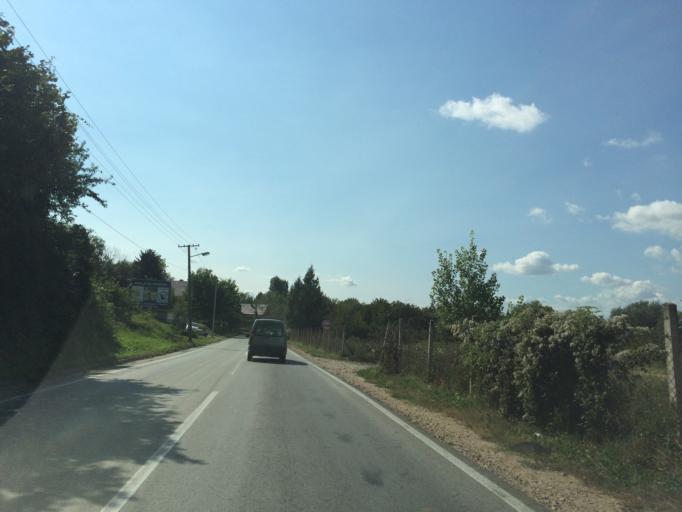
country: RS
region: Autonomna Pokrajina Vojvodina
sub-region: Juznobacki Okrug
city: Novi Sad
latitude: 45.2209
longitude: 19.8313
